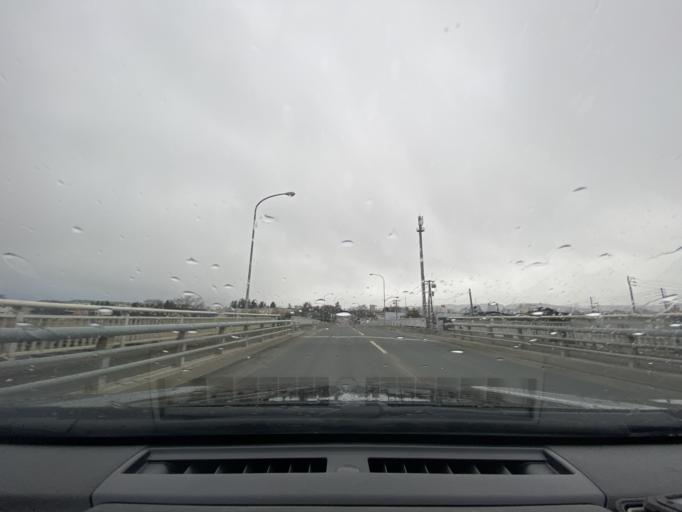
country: JP
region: Hokkaido
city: Kitami
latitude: 43.7992
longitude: 143.9091
